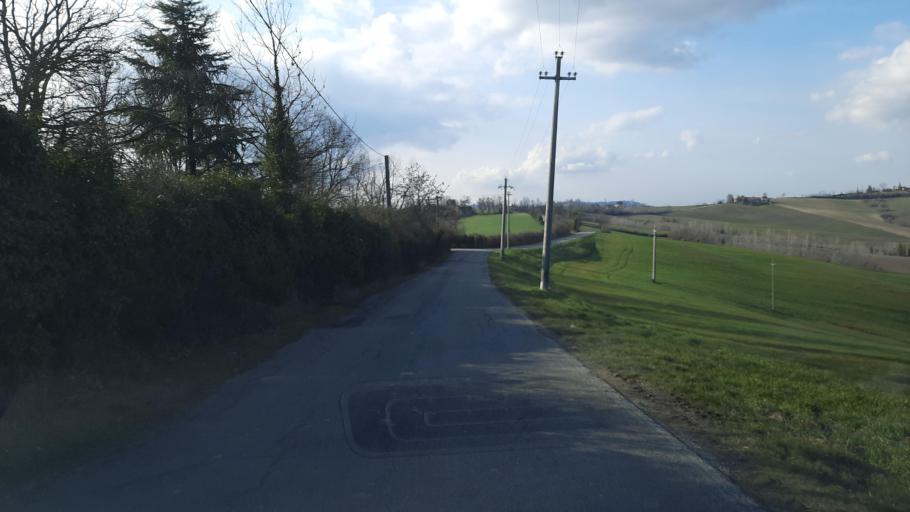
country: IT
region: Piedmont
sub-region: Provincia di Alessandria
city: San Giorgio
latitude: 45.1159
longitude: 8.3948
